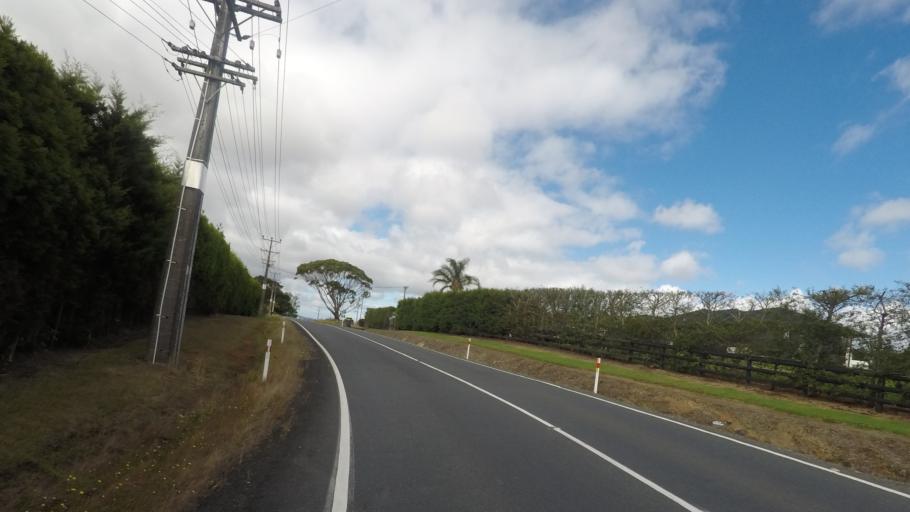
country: NZ
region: Auckland
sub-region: Auckland
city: Muriwai Beach
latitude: -36.7647
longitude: 174.5570
